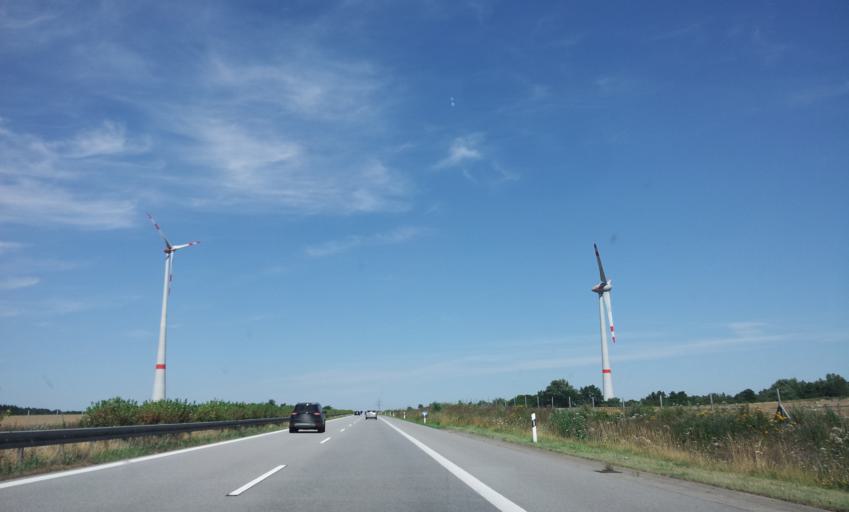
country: DE
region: Mecklenburg-Vorpommern
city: Kessin
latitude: 53.7245
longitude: 13.3340
